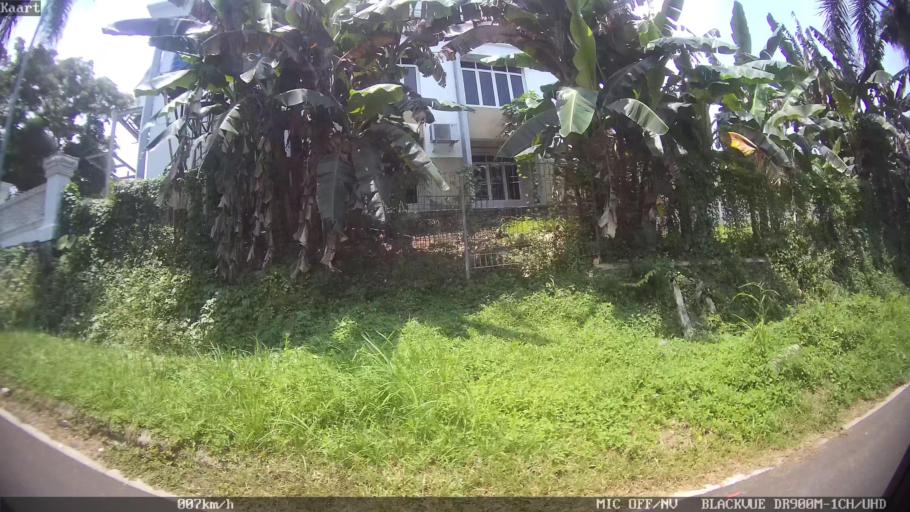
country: ID
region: Lampung
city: Bandarlampung
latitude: -5.4451
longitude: 105.2461
